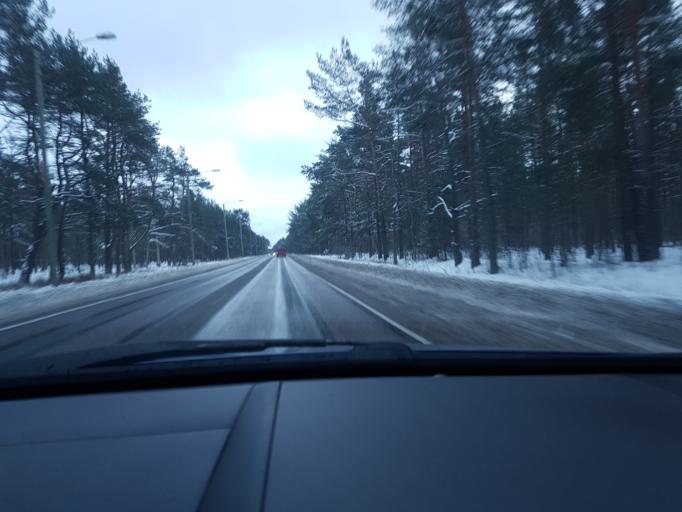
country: EE
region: Harju
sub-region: Tallinna linn
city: Tallinn
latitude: 59.3825
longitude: 24.7396
